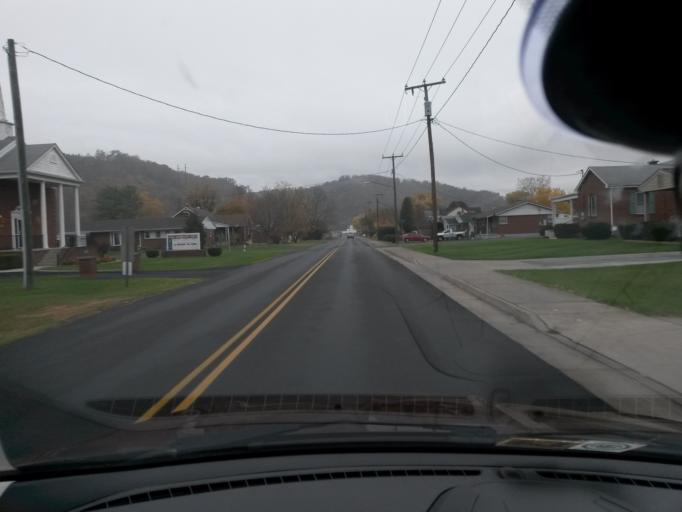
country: US
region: Virginia
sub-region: City of Covington
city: Covington
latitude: 37.7854
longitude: -79.9956
